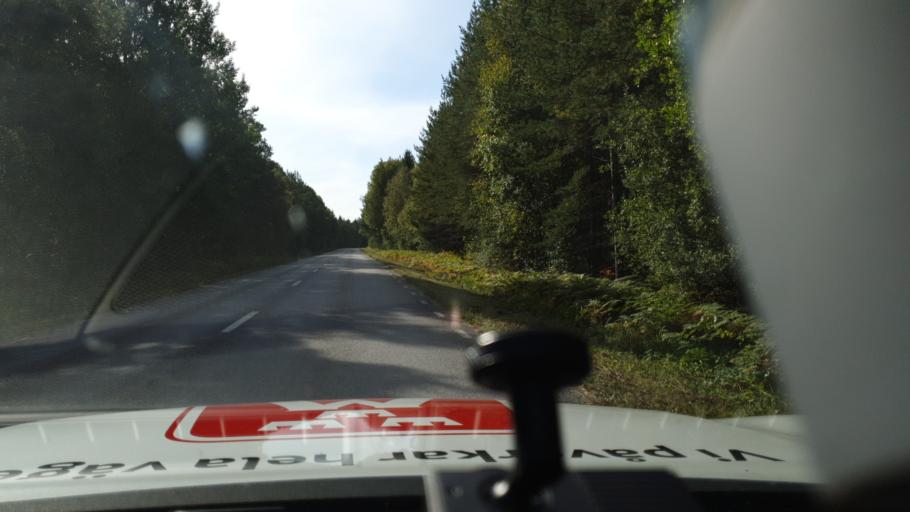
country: SE
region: Gotland
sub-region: Gotland
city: Slite
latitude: 57.8216
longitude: 18.7902
